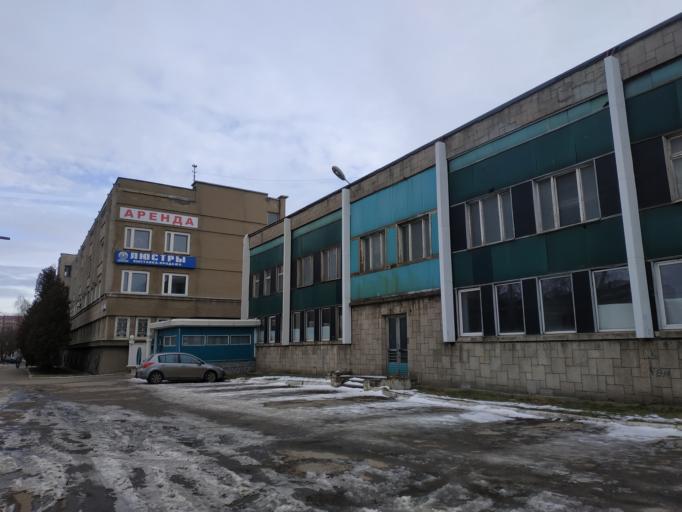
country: RU
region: Tverskaya
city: Tver
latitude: 56.8478
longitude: 35.9348
